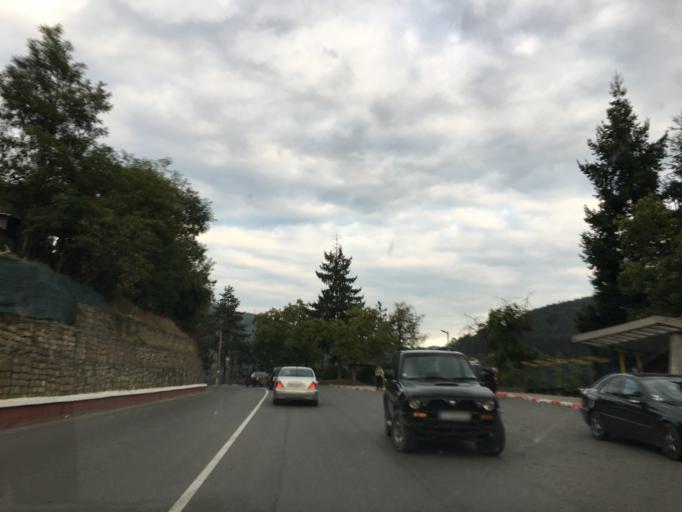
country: BG
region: Sofiya
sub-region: Obshtina Svoge
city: Svoge
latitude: 42.9538
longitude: 23.3631
